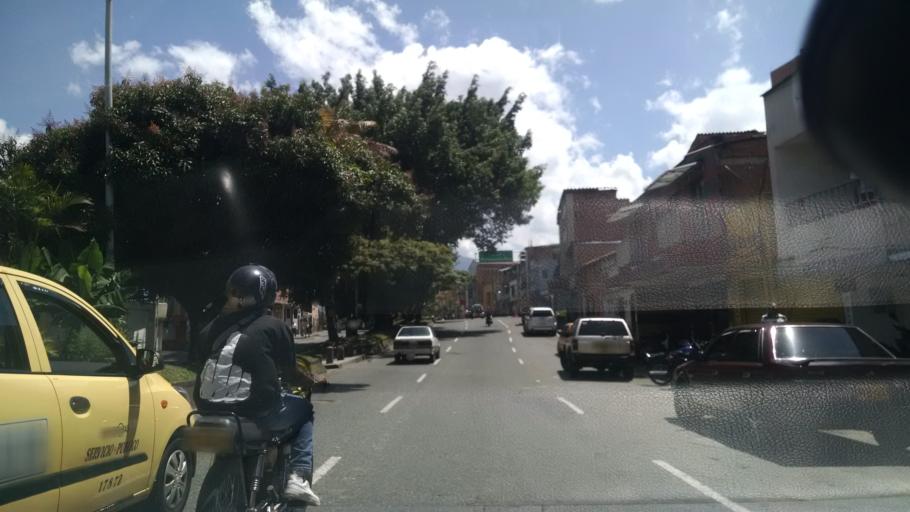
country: CO
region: Antioquia
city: Medellin
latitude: 6.2521
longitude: -75.6074
